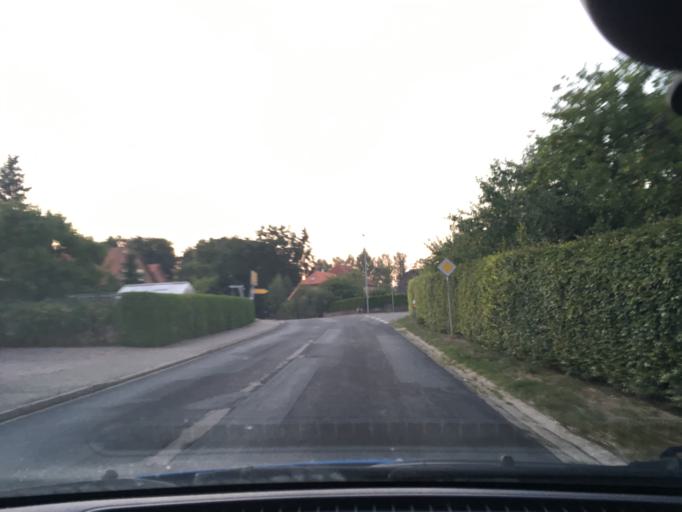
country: DE
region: Lower Saxony
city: Barnstedt
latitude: 53.1408
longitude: 10.3705
